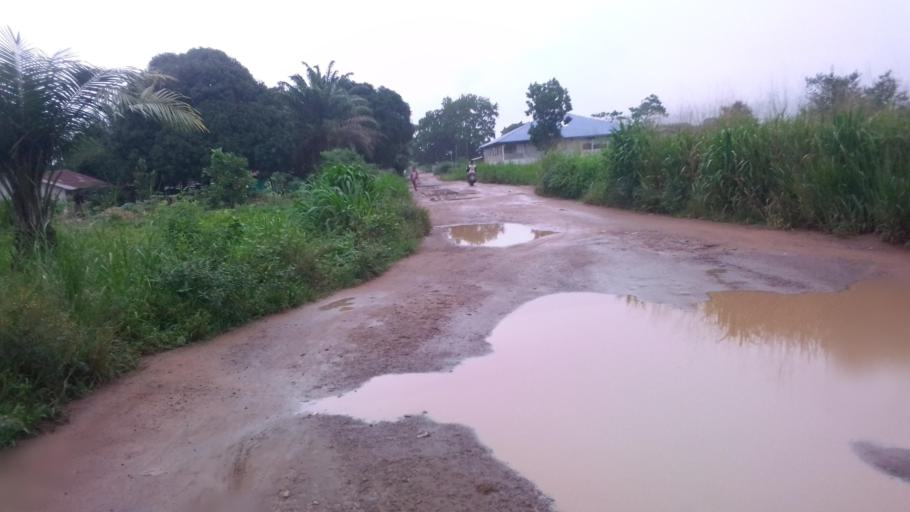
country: SL
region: Eastern Province
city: Kenema
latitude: 7.9000
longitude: -11.1694
